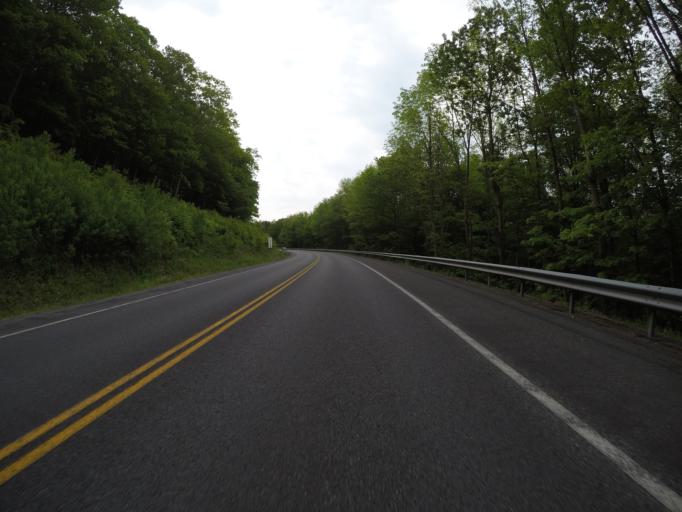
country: US
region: New York
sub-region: Sullivan County
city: Livingston Manor
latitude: 42.0493
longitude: -74.9129
